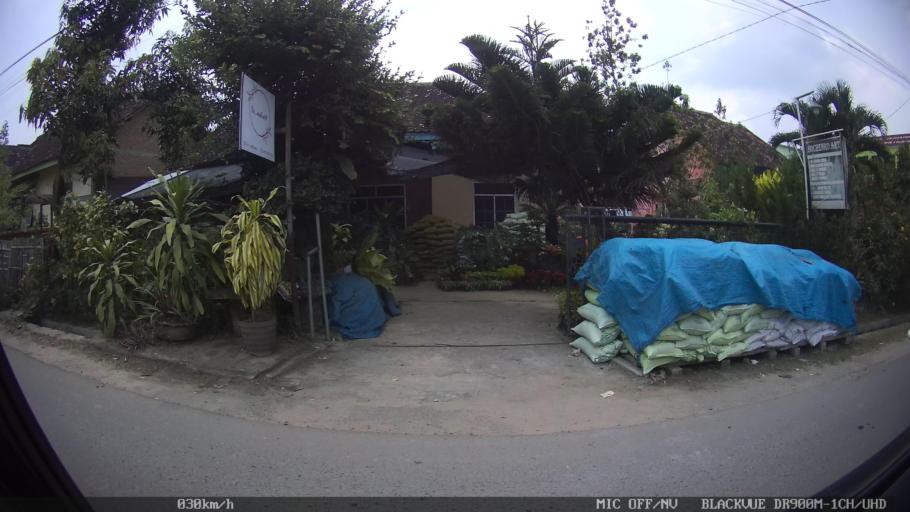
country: ID
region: Lampung
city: Pringsewu
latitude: -5.3529
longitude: 104.9797
